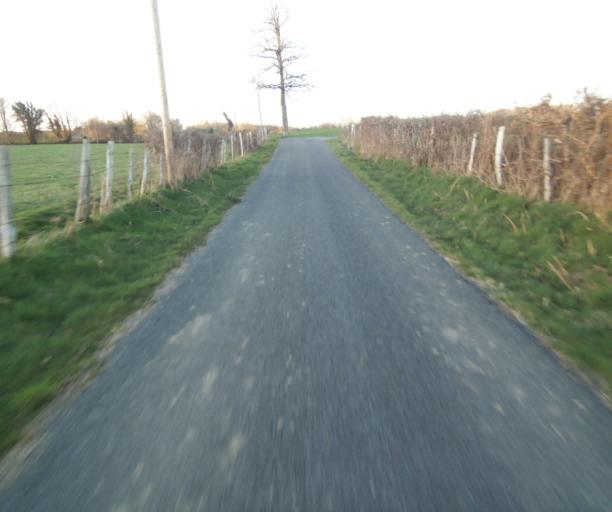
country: FR
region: Limousin
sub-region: Departement de la Correze
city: Saint-Clement
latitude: 45.3706
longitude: 1.6185
